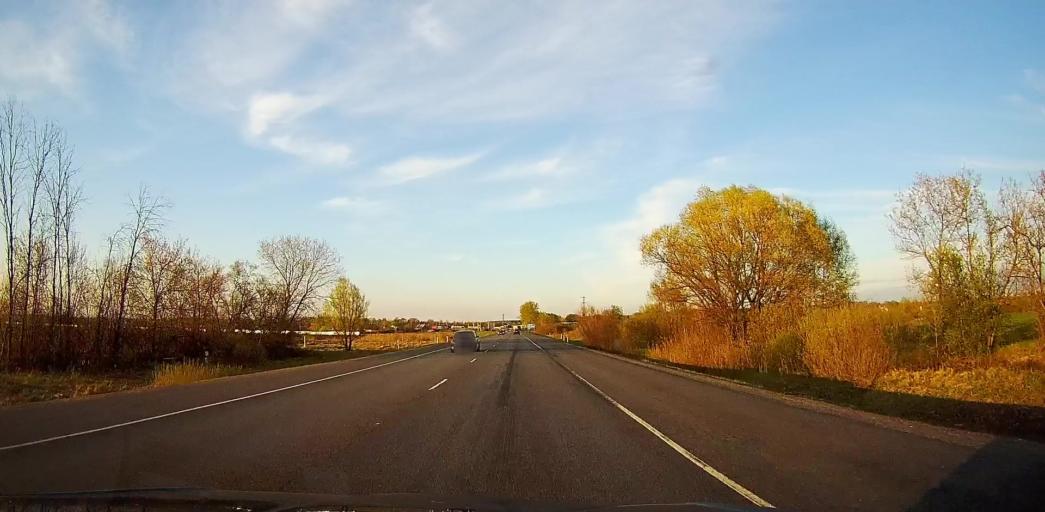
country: RU
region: Moskovskaya
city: Troitskoye
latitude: 55.2735
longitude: 38.4848
